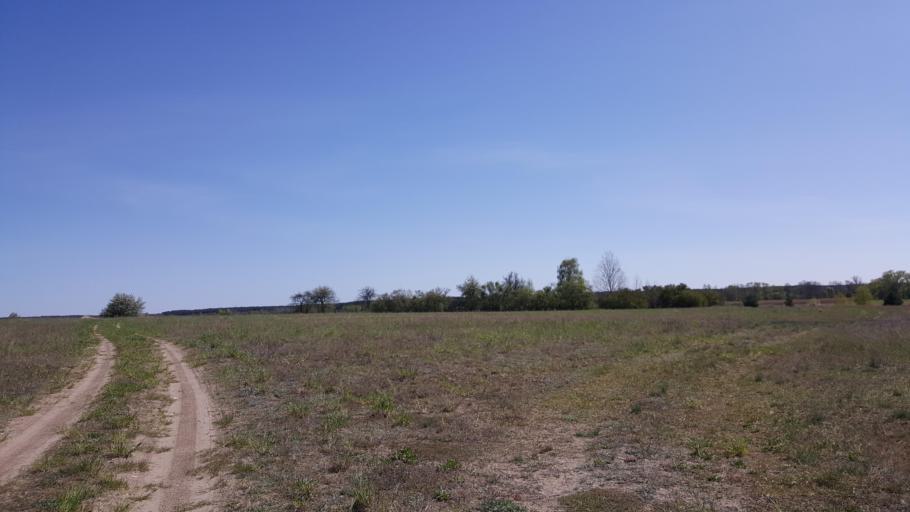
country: BY
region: Brest
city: Kamyanyets
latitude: 52.4468
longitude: 23.9015
